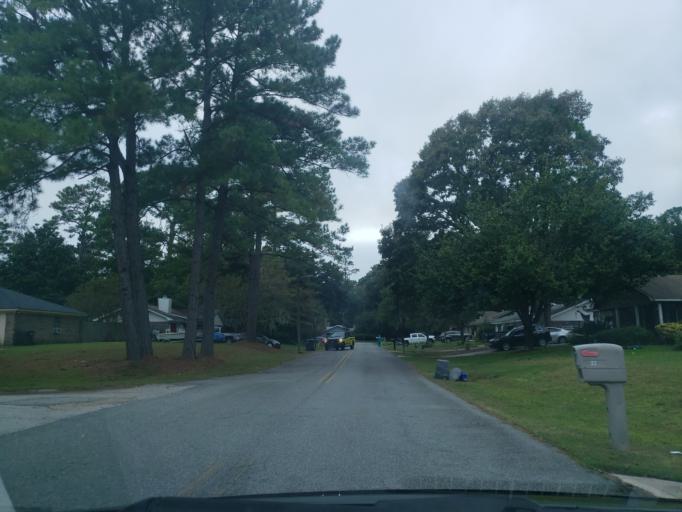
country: US
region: Georgia
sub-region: Chatham County
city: Montgomery
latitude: 31.9537
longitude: -81.1097
